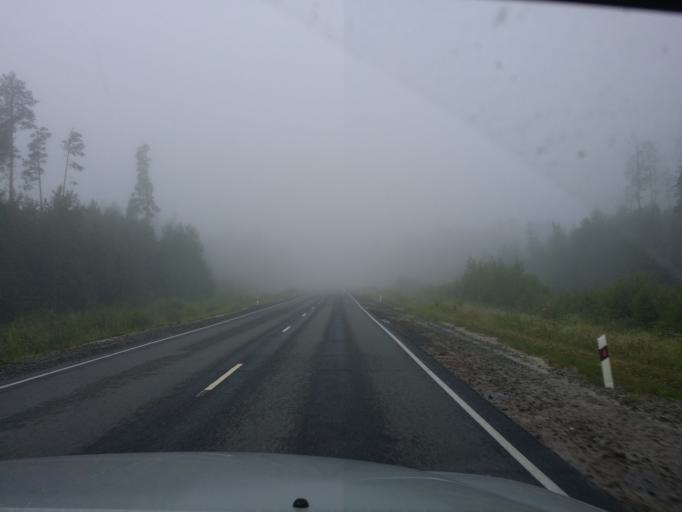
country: RU
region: Khanty-Mansiyskiy Avtonomnyy Okrug
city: Gornopravdinsk
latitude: 59.6595
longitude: 69.9569
